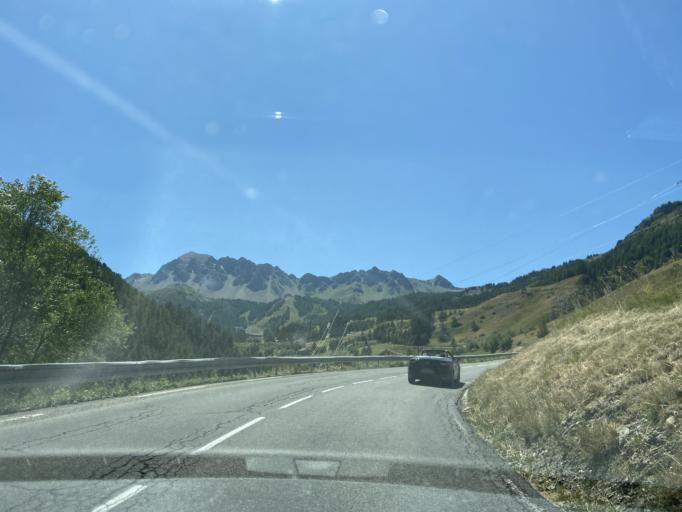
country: FR
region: Provence-Alpes-Cote d'Azur
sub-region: Departement des Hautes-Alpes
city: Guillestre
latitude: 44.5868
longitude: 6.6866
